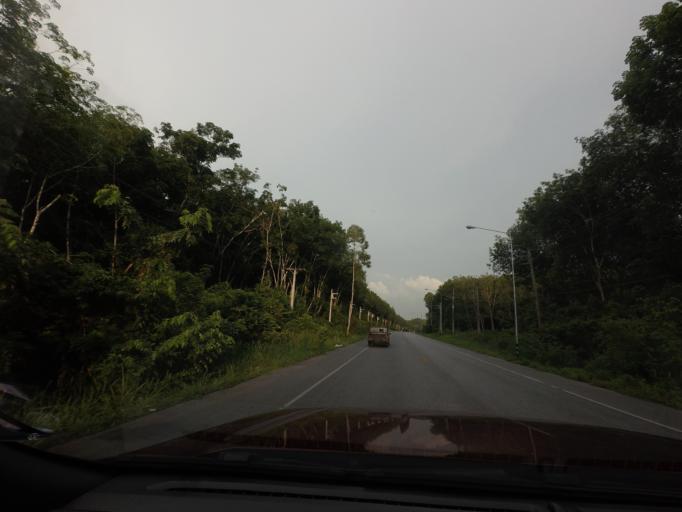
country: TH
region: Pattani
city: Mae Lan
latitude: 6.6721
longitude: 101.1567
